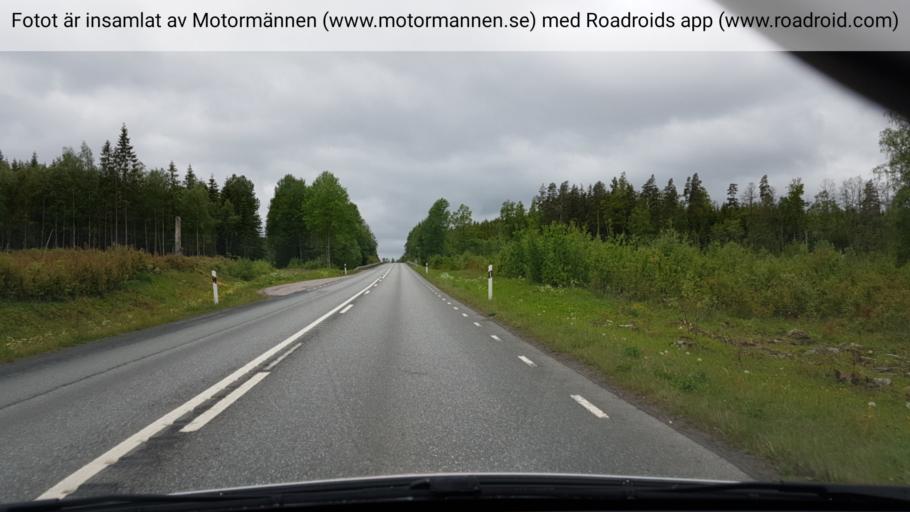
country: SE
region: Joenkoeping
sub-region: Jonkopings Kommun
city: Asa
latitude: 58.0123
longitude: 14.6578
